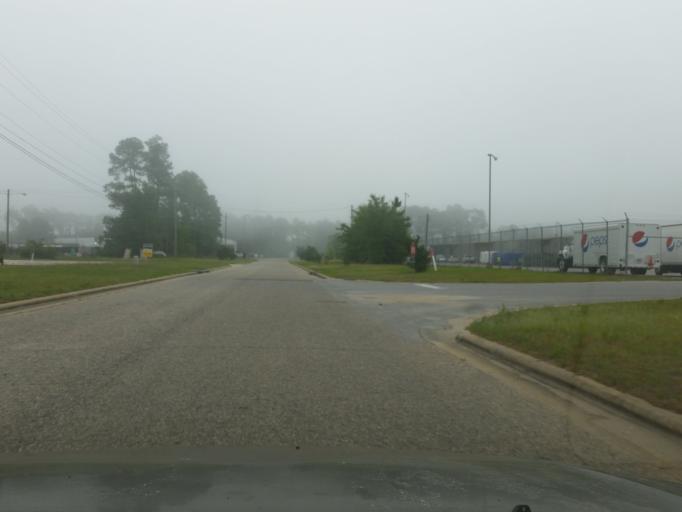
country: US
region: Florida
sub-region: Escambia County
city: Ferry Pass
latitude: 30.5234
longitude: -87.1929
